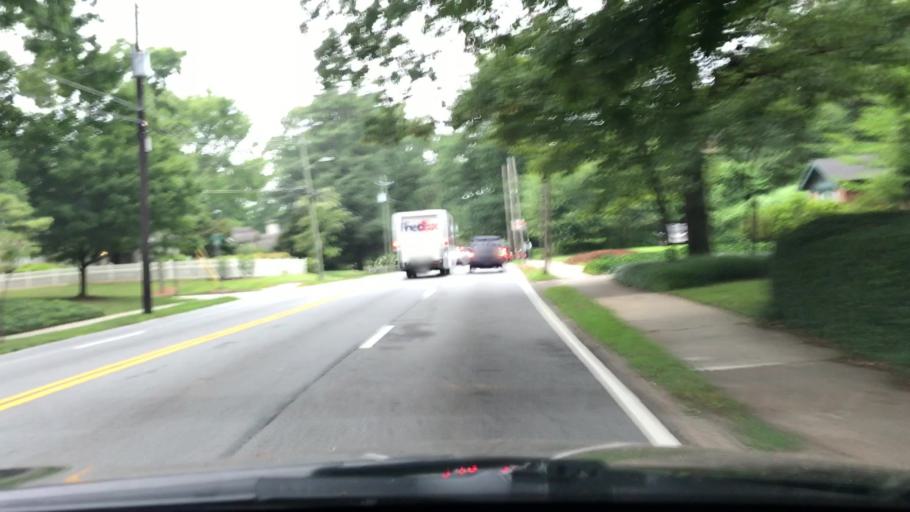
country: US
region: Georgia
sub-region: DeKalb County
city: North Decatur
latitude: 33.7833
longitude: -84.3016
